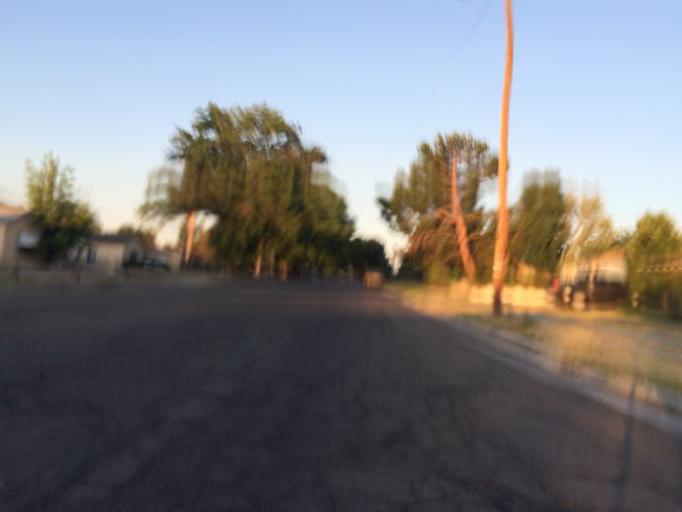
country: US
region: California
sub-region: Fresno County
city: Fresno
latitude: 36.7759
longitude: -119.7832
